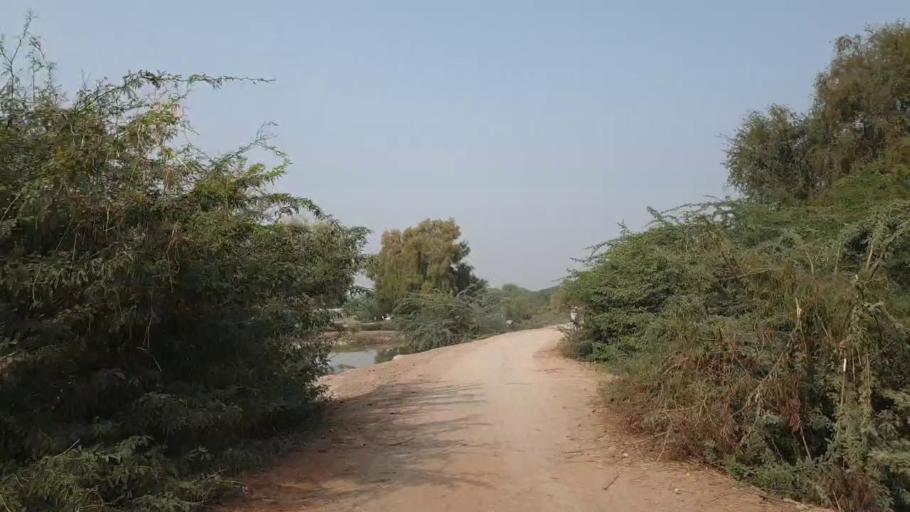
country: PK
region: Sindh
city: Bhan
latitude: 26.5402
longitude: 67.7013
